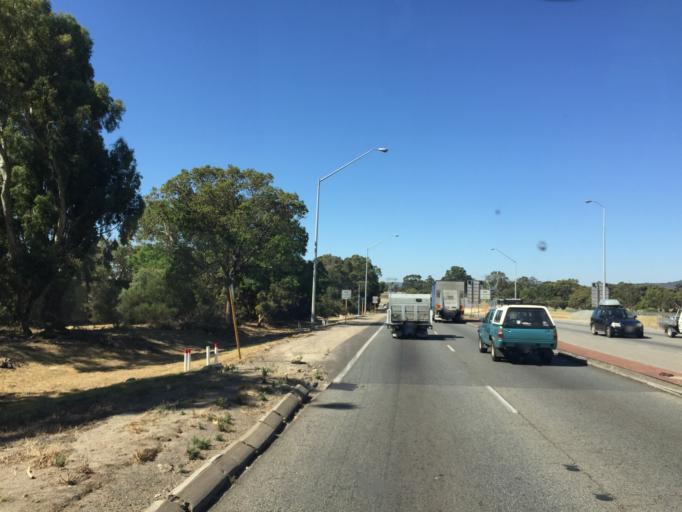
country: AU
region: Western Australia
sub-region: Kalamunda
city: Maida Vale
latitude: -31.9402
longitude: 116.0162
